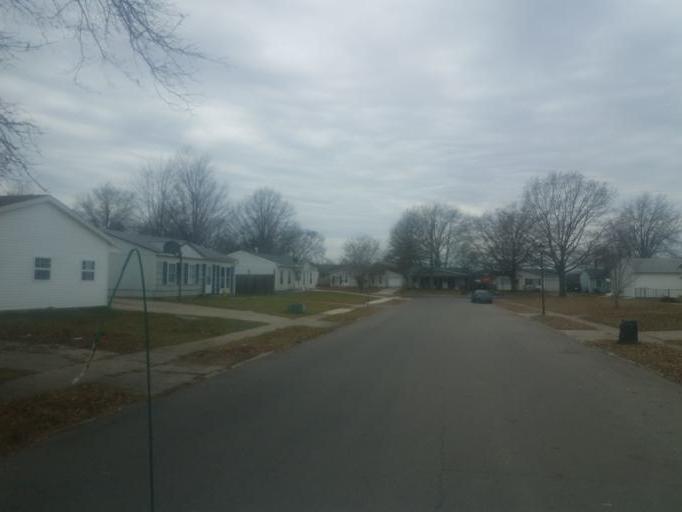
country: US
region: Ohio
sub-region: Marion County
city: Marion
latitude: 40.6116
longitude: -83.1116
